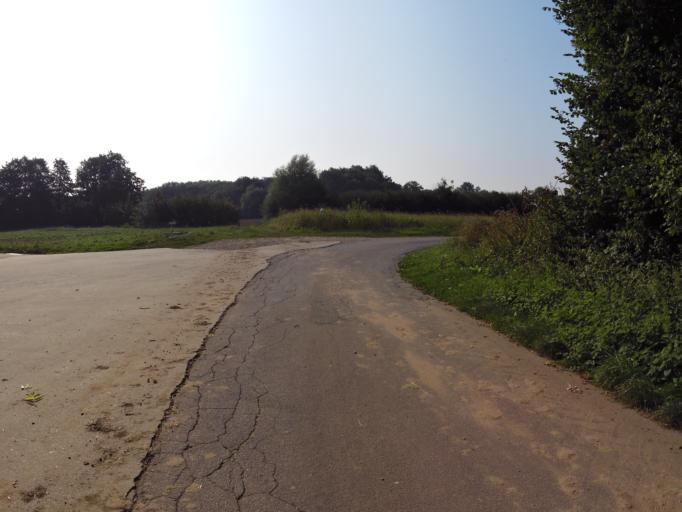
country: DE
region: North Rhine-Westphalia
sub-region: Regierungsbezirk Munster
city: Havixbeck
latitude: 51.9817
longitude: 7.3848
